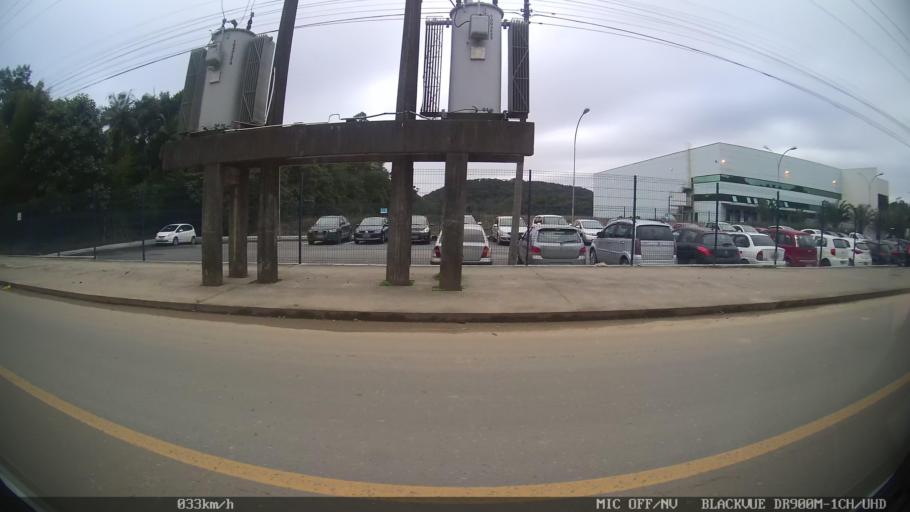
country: BR
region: Santa Catarina
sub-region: Joinville
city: Joinville
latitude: -26.2541
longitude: -48.9248
